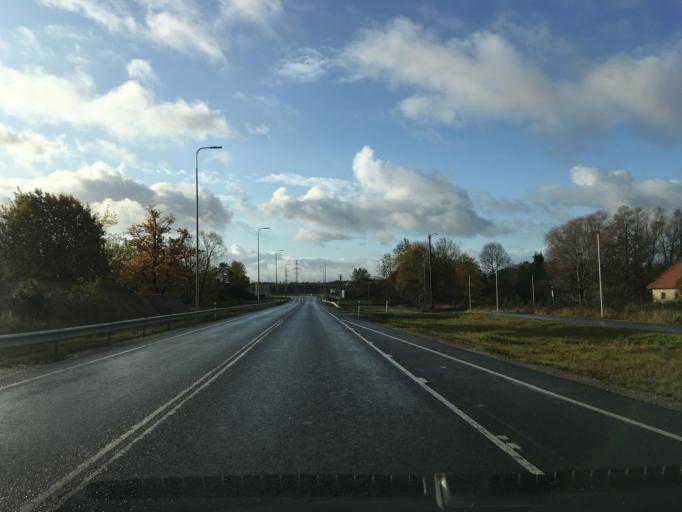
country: EE
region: Harju
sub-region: Saue vald
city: Laagri
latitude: 59.3522
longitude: 24.5994
